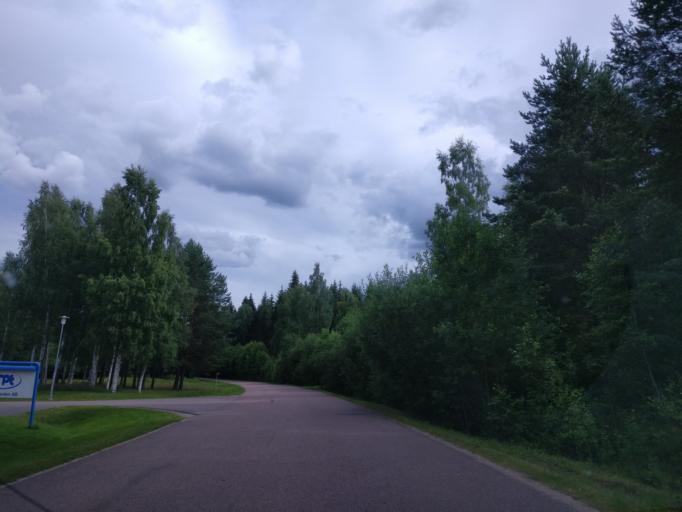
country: SE
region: Vaermland
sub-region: Hagfors Kommun
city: Ekshaerad
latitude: 60.1625
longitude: 13.4991
